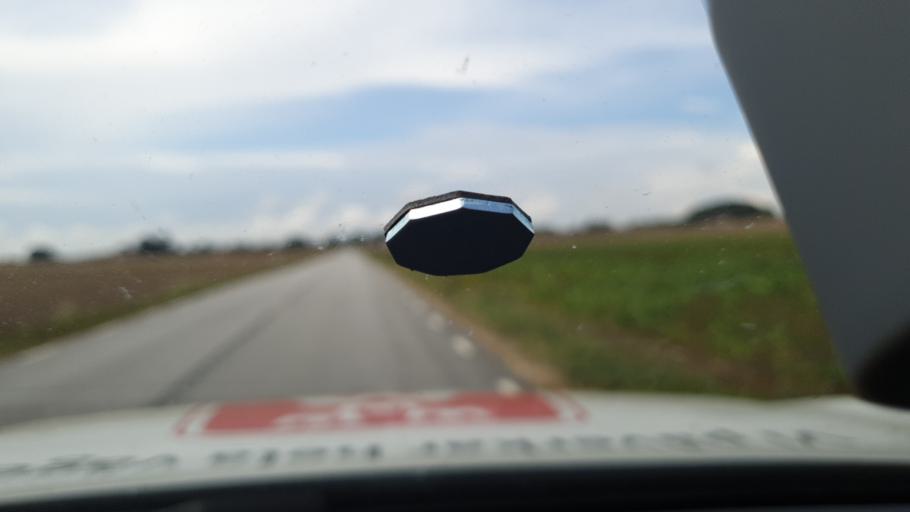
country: SE
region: Skane
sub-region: Simrishamns Kommun
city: Simrishamn
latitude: 55.4652
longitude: 14.2016
